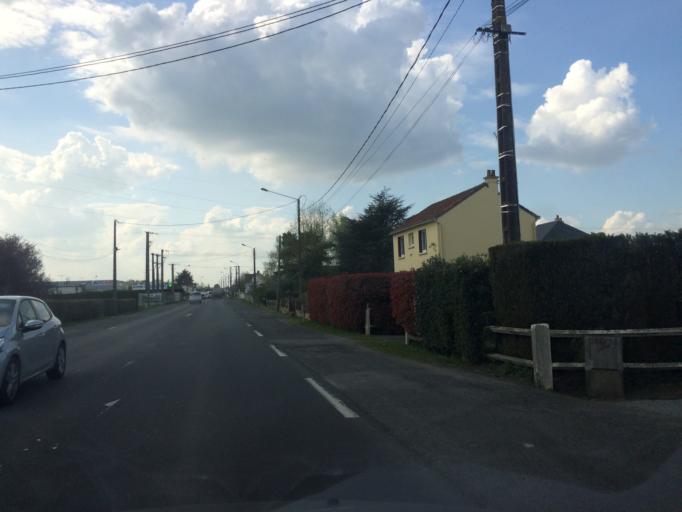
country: FR
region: Pays de la Loire
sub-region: Departement de la Loire-Atlantique
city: Blain
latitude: 47.4725
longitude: -1.7432
